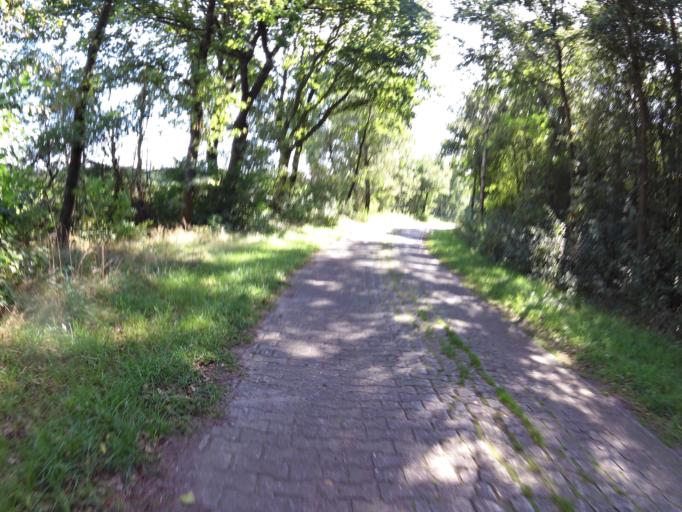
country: DE
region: Lower Saxony
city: Sandbostel
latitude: 53.3880
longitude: 9.1262
